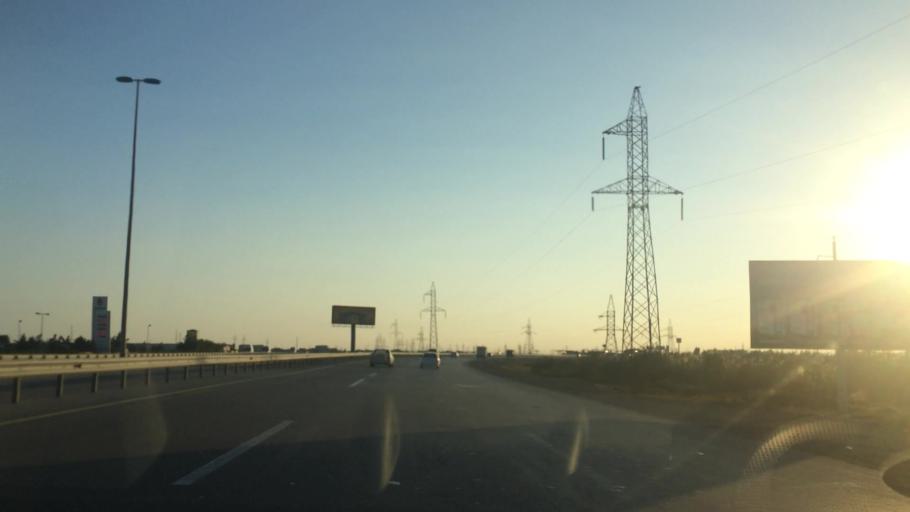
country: AZ
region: Baki
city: Qobustan
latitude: 39.9711
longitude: 49.4156
